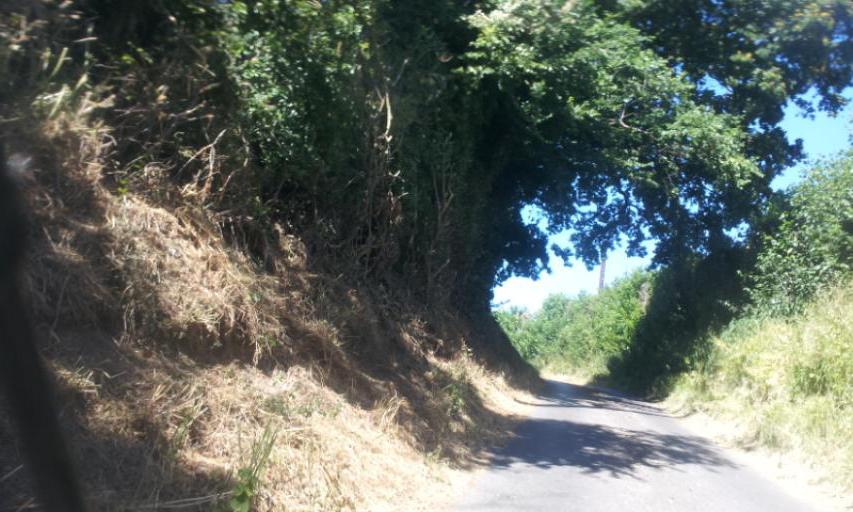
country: GB
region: England
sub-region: Kent
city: Teynham
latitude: 51.3478
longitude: 0.7807
